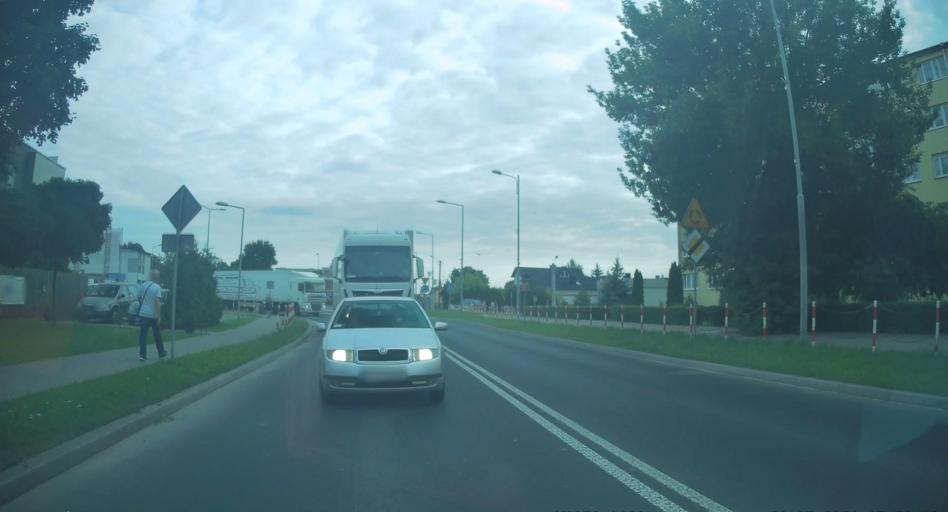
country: PL
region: Lodz Voivodeship
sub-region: Powiat radomszczanski
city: Radomsko
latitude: 51.0629
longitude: 19.4425
